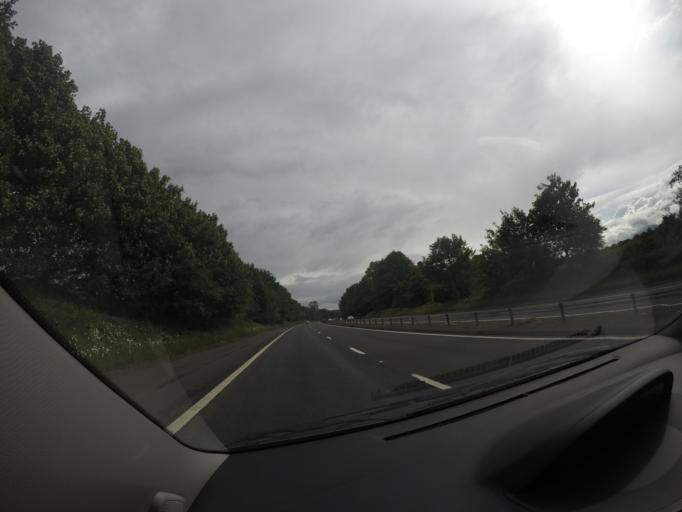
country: GB
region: Scotland
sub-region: Falkirk
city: Dunipace
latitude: 56.0447
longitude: -3.9175
